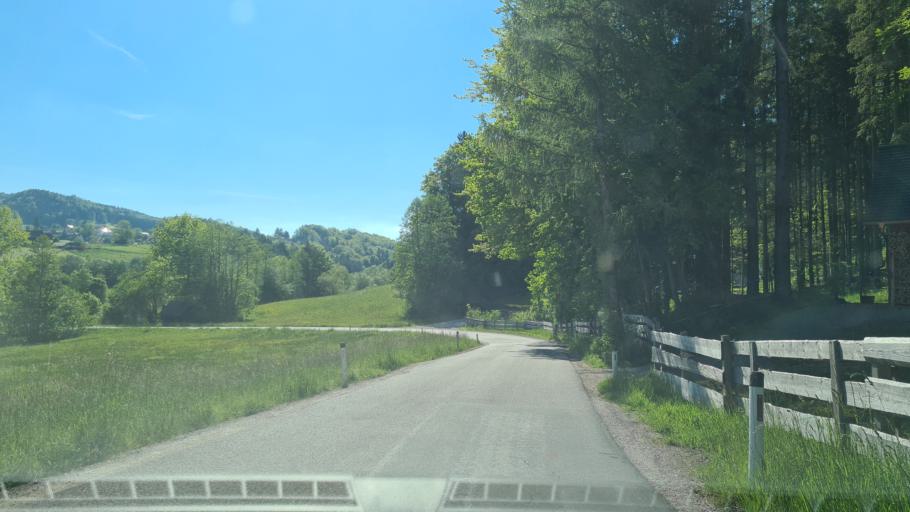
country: AT
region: Salzburg
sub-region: Politischer Bezirk Salzburg-Umgebung
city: Thalgau
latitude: 47.8205
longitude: 13.2464
